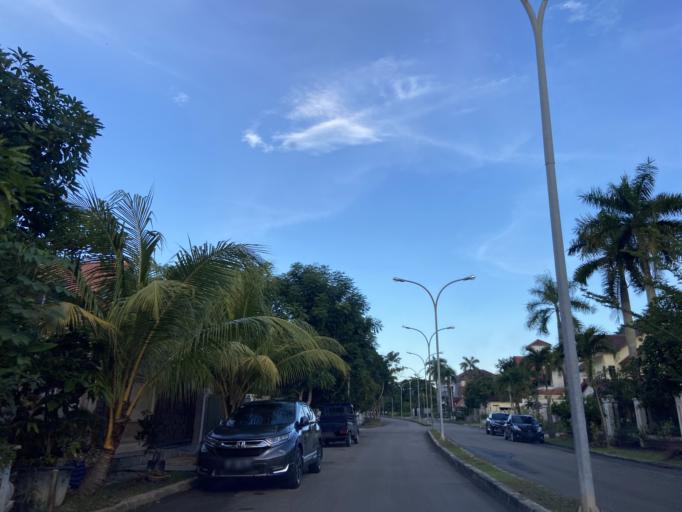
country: SG
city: Singapore
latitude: 1.1085
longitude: 104.0263
